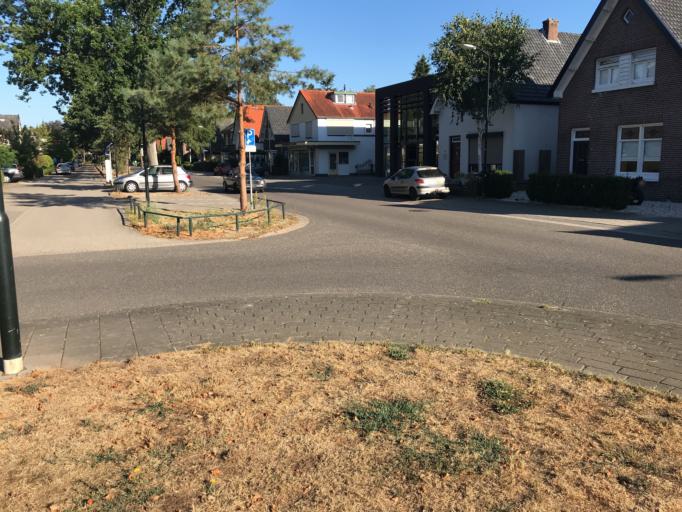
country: NL
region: Gelderland
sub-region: Gemeente Apeldoorn
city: Apeldoorn
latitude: 52.2150
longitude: 5.9404
